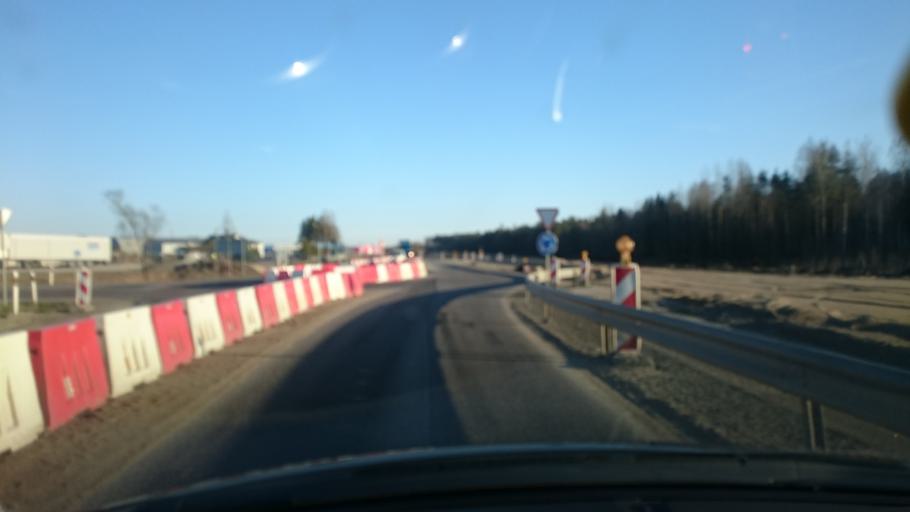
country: EE
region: Harju
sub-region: Joelaehtme vald
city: Loo
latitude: 59.4033
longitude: 24.9160
